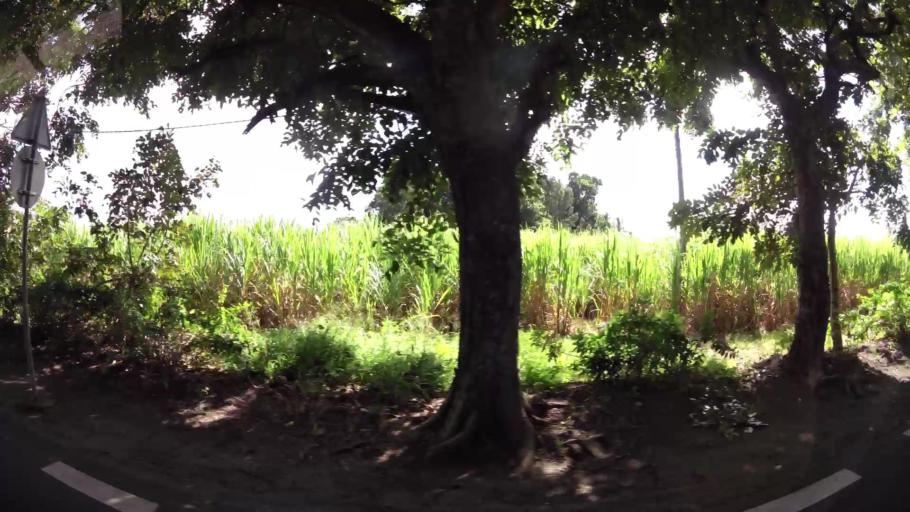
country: MU
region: Grand Port
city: Beau Vallon
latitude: -20.4240
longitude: 57.6998
